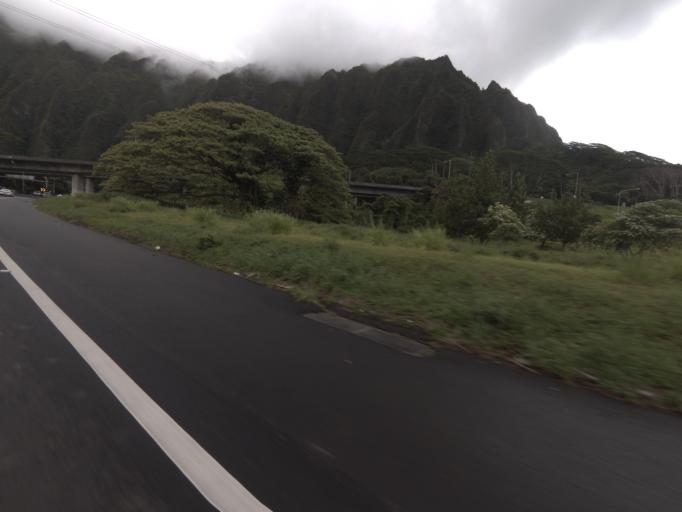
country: US
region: Hawaii
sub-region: Honolulu County
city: Kane'ohe
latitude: 21.3941
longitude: -157.8119
